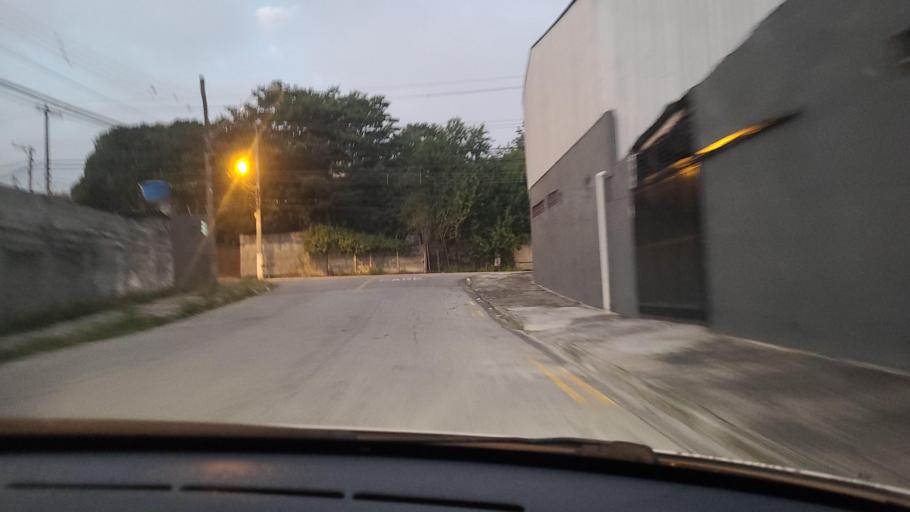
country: BR
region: Sao Paulo
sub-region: Pindamonhangaba
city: Pindamonhangaba
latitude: -22.9189
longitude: -45.4437
